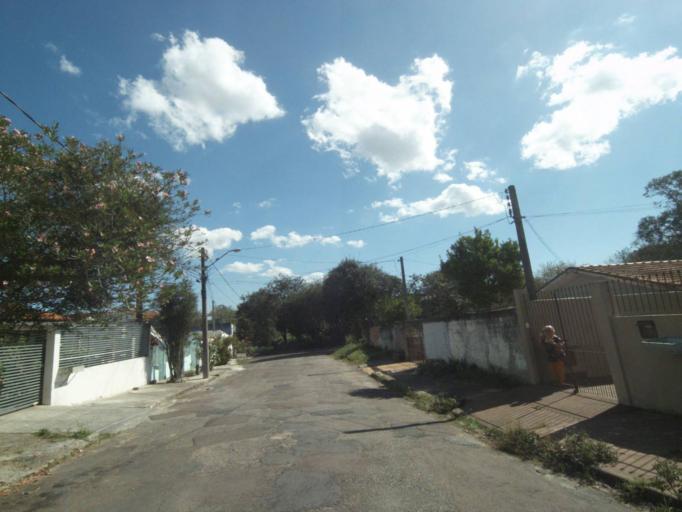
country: BR
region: Parana
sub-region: Curitiba
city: Curitiba
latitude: -25.3792
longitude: -49.2480
